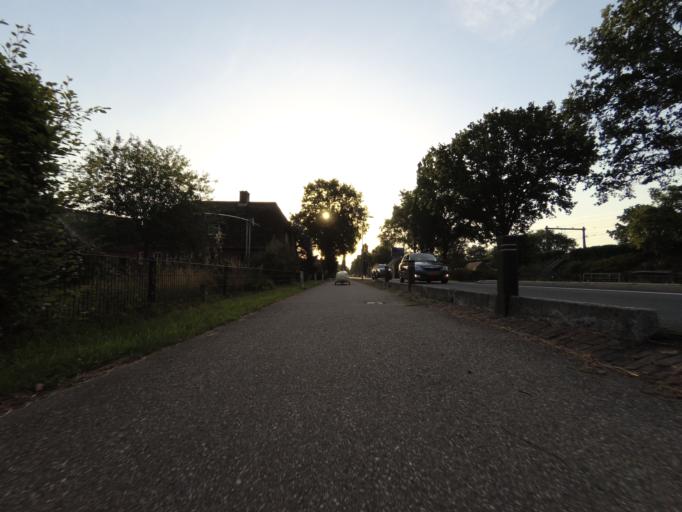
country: NL
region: Gelderland
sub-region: Gemeente Lochem
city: Laren
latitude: 52.2828
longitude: 6.4104
